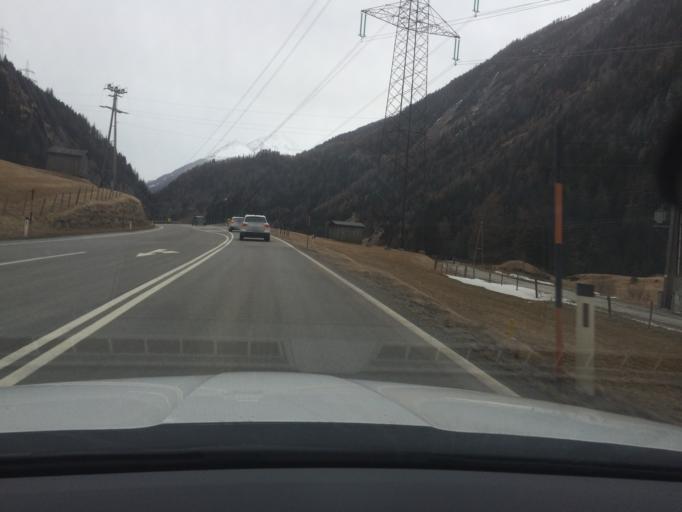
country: AT
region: Tyrol
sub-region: Politischer Bezirk Lienz
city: Matrei in Osttirol
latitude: 47.0389
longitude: 12.5173
